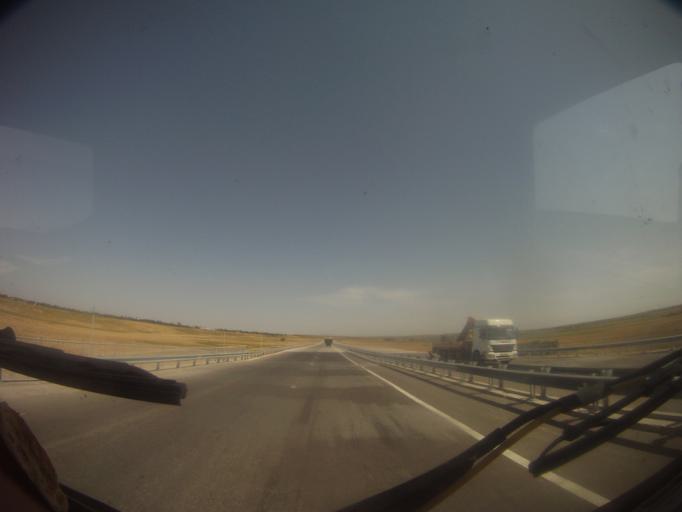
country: KZ
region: Ongtustik Qazaqstan
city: Aksu
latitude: 42.4433
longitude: 69.6887
